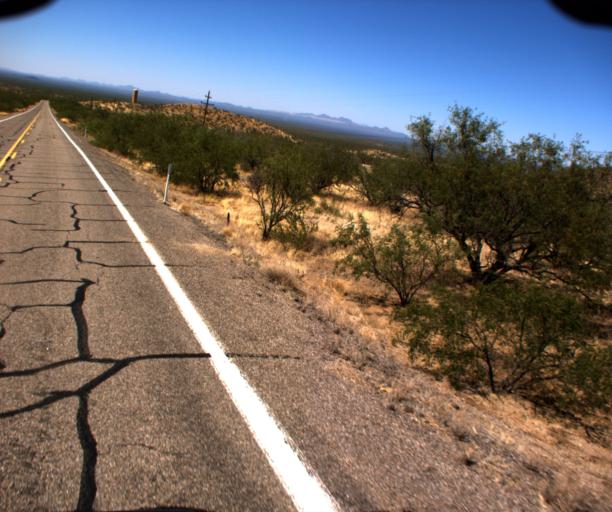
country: US
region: Arizona
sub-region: Pima County
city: Three Points
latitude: 31.9996
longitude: -111.5711
